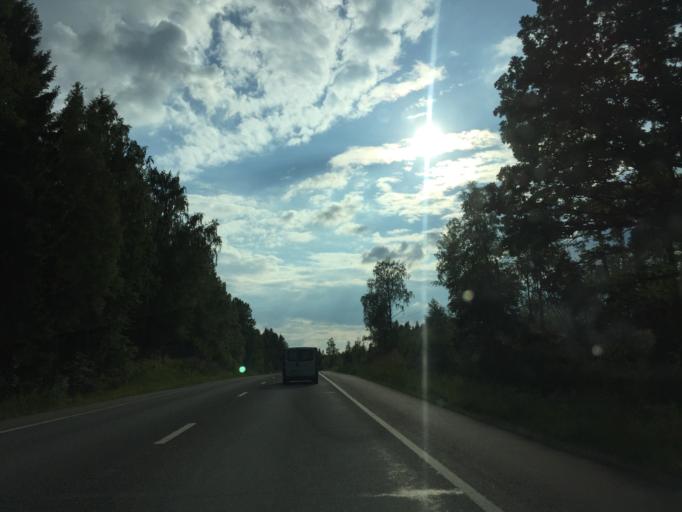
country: SE
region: Vaestmanland
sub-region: Arboga Kommun
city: Arboga
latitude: 59.3756
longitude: 15.7535
